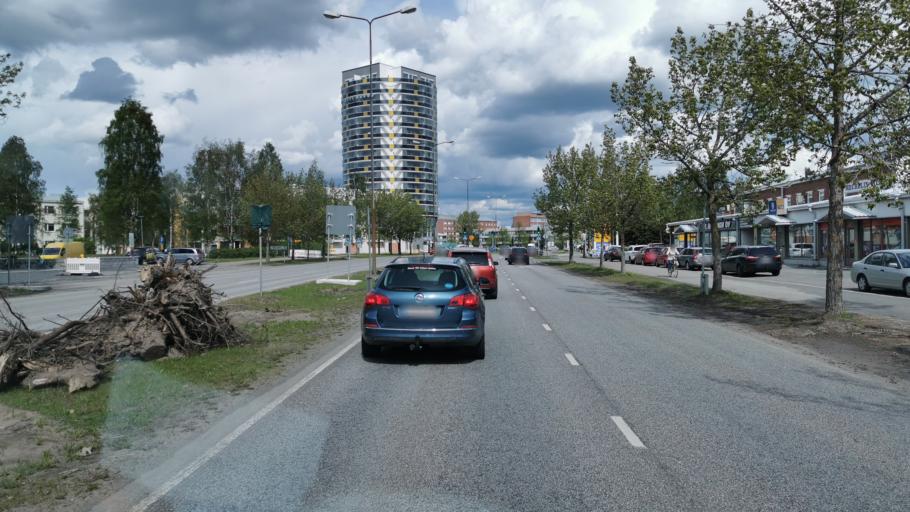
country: FI
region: Northern Ostrobothnia
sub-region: Oulu
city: Oulu
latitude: 65.0019
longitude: 25.4637
